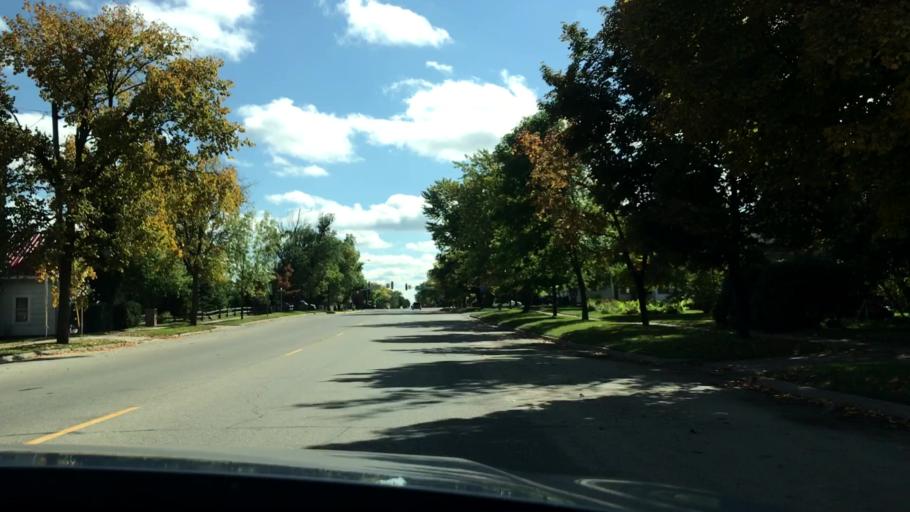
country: US
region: Minnesota
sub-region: Hubbard County
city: Park Rapids
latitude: 46.9242
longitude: -95.0586
